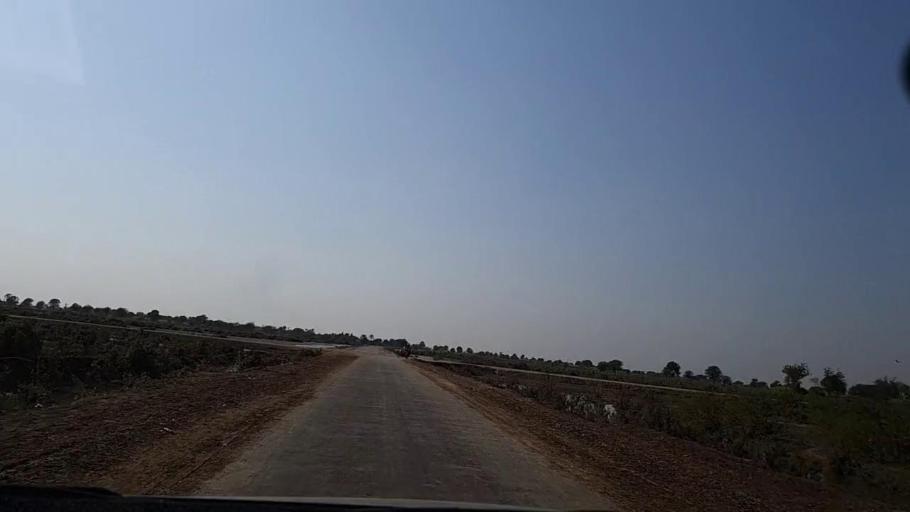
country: PK
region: Sindh
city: Digri
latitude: 25.1736
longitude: 69.0495
